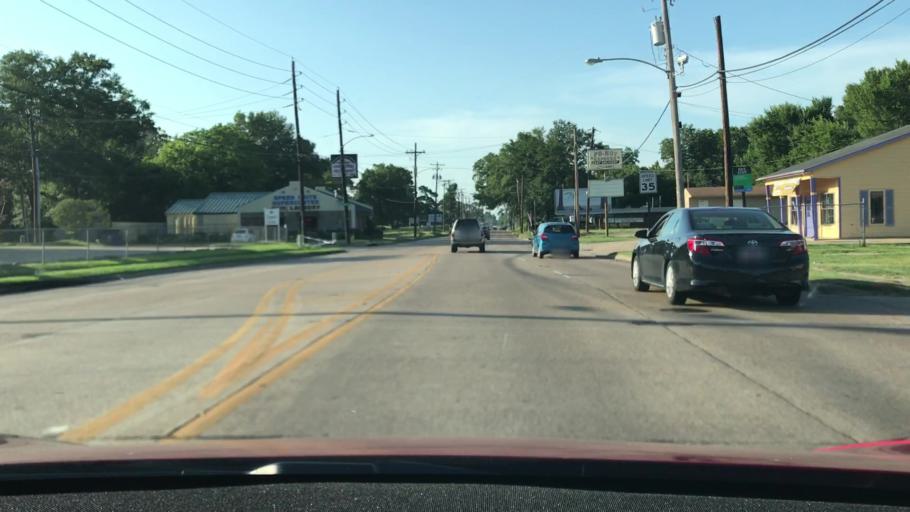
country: US
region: Louisiana
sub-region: Bossier Parish
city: Bossier City
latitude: 32.4425
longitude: -93.7459
